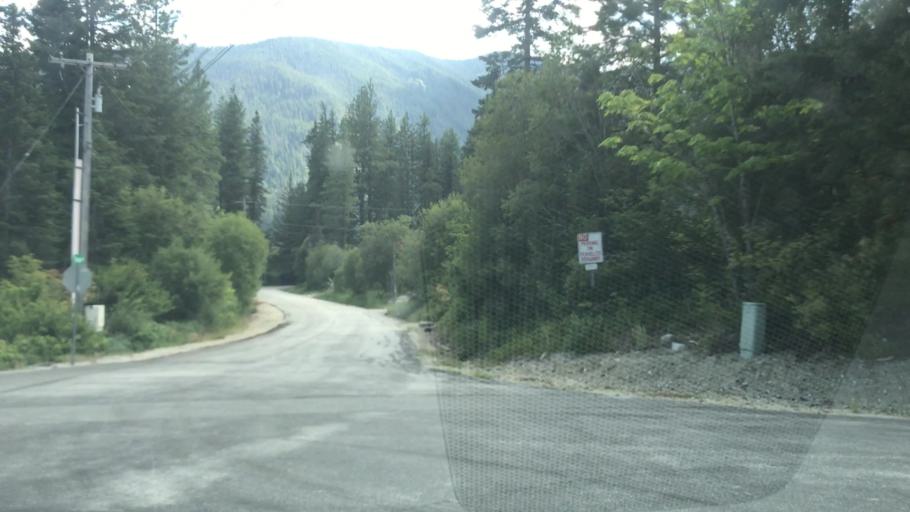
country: US
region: Washington
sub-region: Chelan County
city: Leavenworth
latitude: 47.8320
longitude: -120.7752
